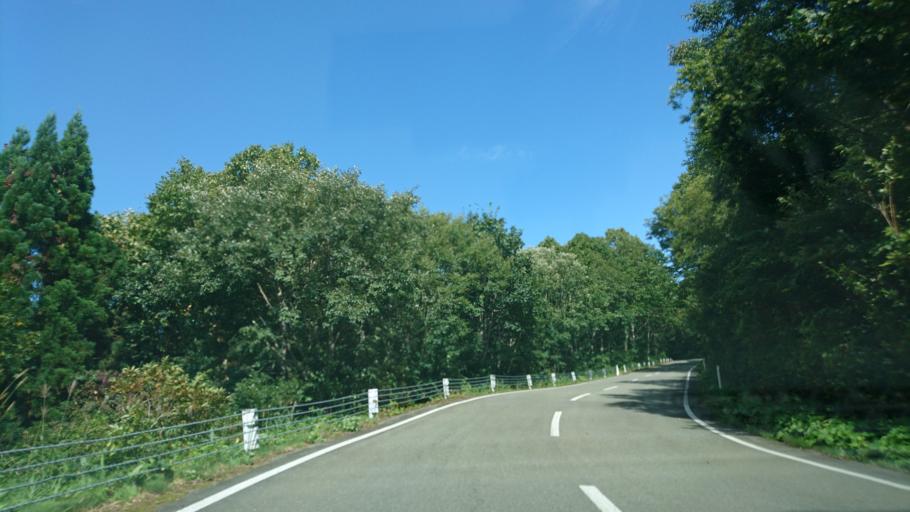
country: JP
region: Akita
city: Yuzawa
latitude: 38.9679
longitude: 140.7122
